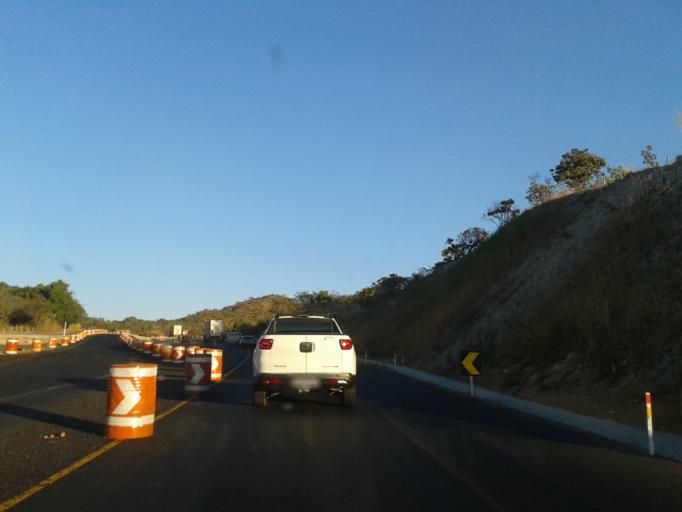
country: BR
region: Goias
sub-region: Goias
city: Goias
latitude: -15.9985
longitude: -50.0737
